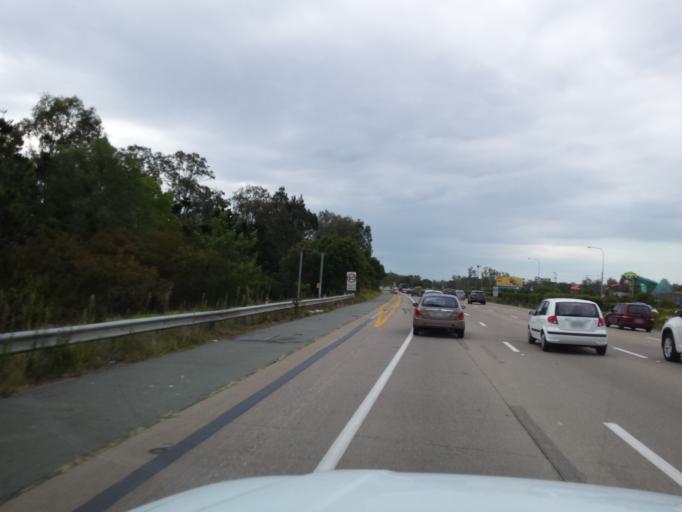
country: AU
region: Queensland
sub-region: Gold Coast
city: Oxenford
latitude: -27.8687
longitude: 153.3129
